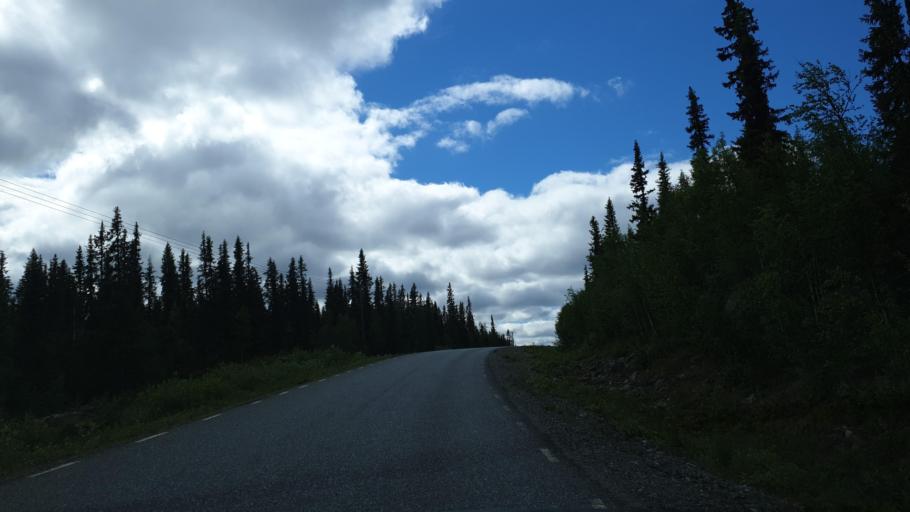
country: SE
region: Vaesterbotten
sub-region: Vilhelmina Kommun
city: Sjoberg
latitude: 65.1880
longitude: 15.9437
